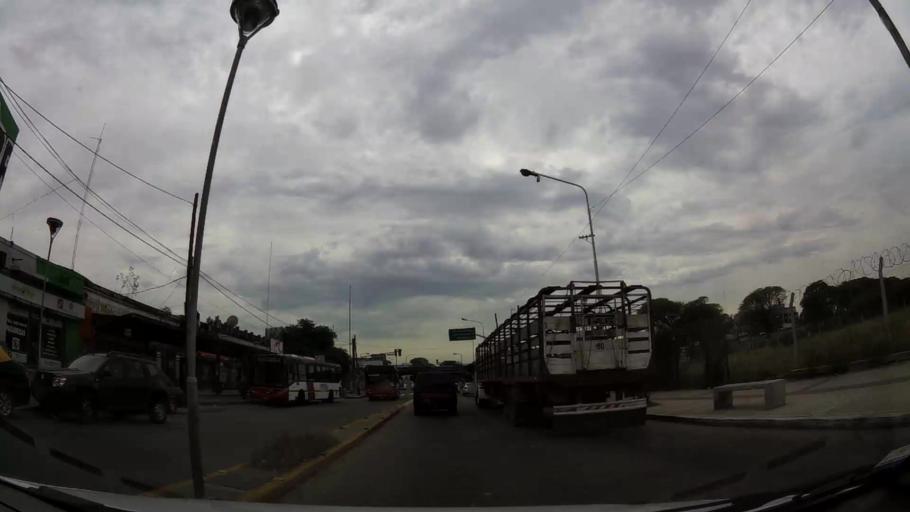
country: AR
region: Buenos Aires F.D.
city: Villa Lugano
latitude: -34.6748
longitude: -58.5032
